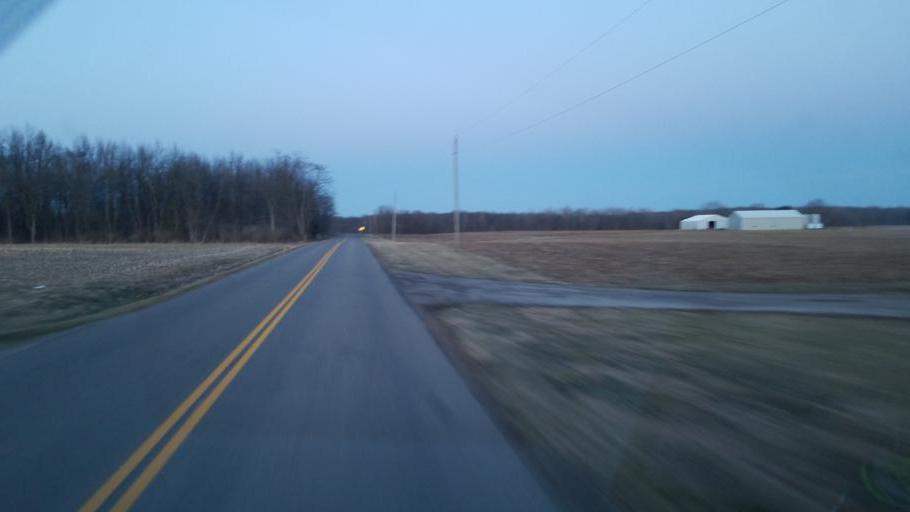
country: US
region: Ohio
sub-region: Champaign County
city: North Lewisburg
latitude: 40.2638
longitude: -83.5607
